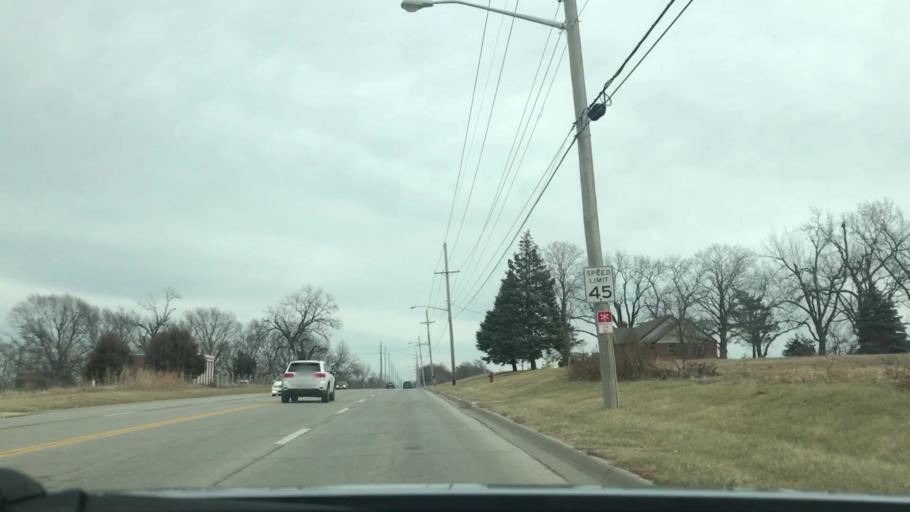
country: US
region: Kansas
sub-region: Leavenworth County
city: Basehor
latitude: 39.1286
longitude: -94.8716
